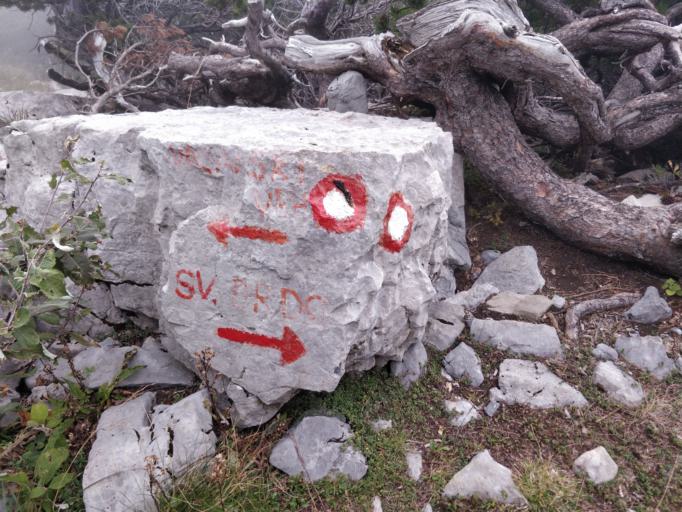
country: HR
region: Zadarska
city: Starigrad
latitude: 44.3596
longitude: 15.5152
